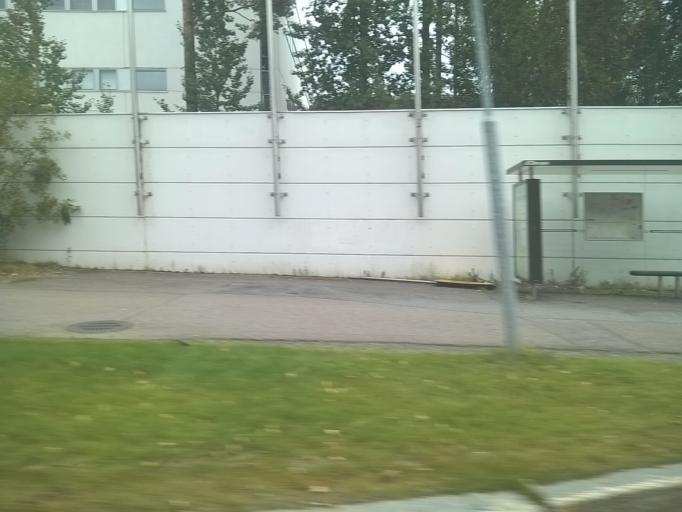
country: FI
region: Pirkanmaa
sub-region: Tampere
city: Tampere
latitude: 61.4527
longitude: 23.8512
